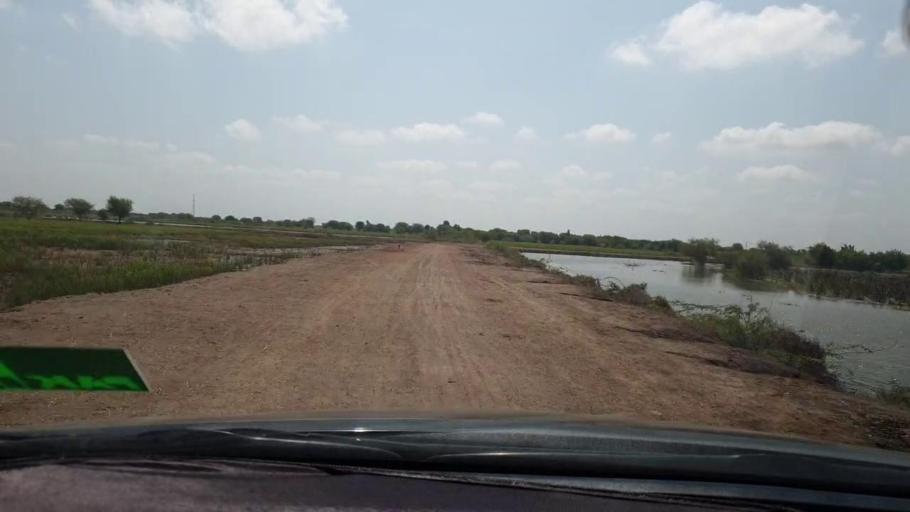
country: PK
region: Sindh
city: Tando Bago
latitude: 24.9350
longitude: 69.0944
